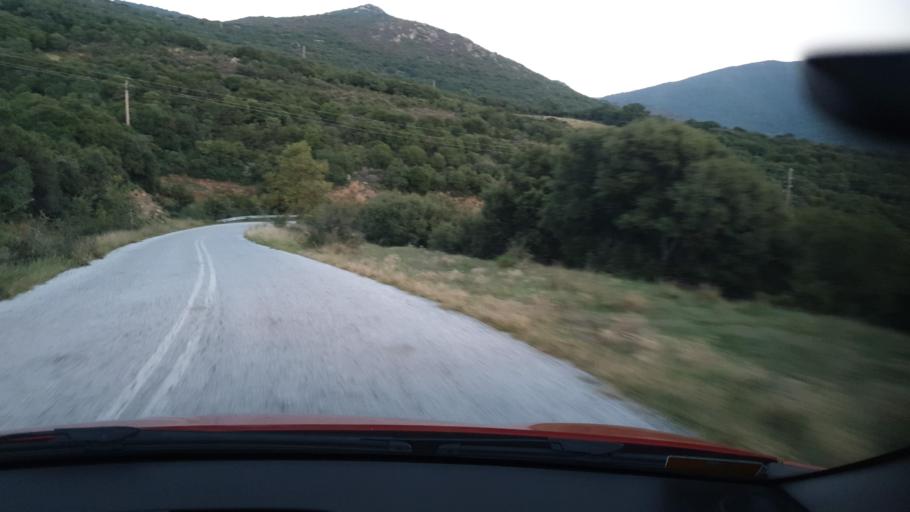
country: GR
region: Central Macedonia
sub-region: Nomos Thessalonikis
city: Peristera
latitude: 40.5237
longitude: 23.1878
